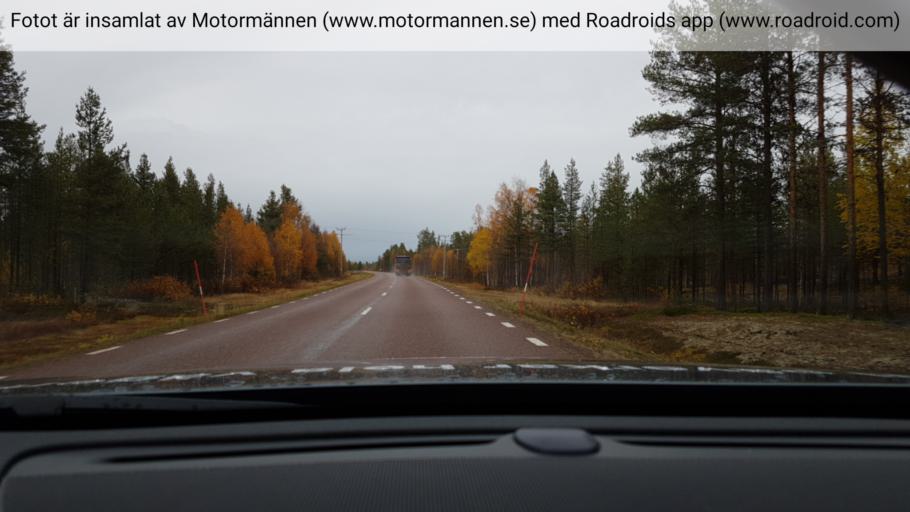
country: SE
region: Norrbotten
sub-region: Pajala Kommun
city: Pajala
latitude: 67.1749
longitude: 22.6923
